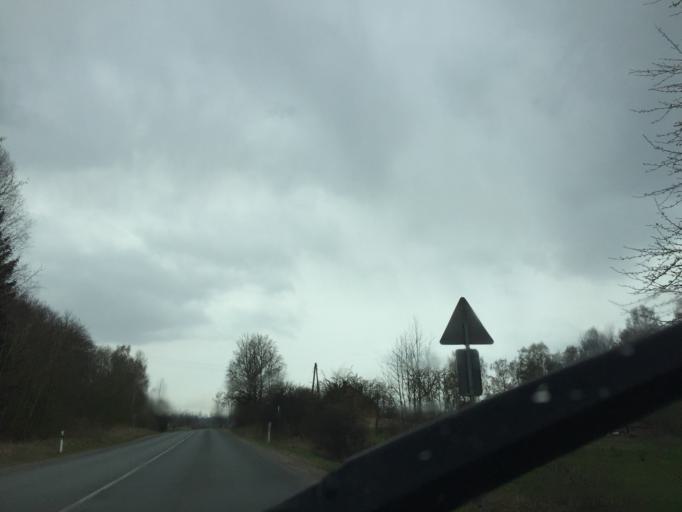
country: LV
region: Priekuli
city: Priekuli
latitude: 57.3439
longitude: 25.3388
